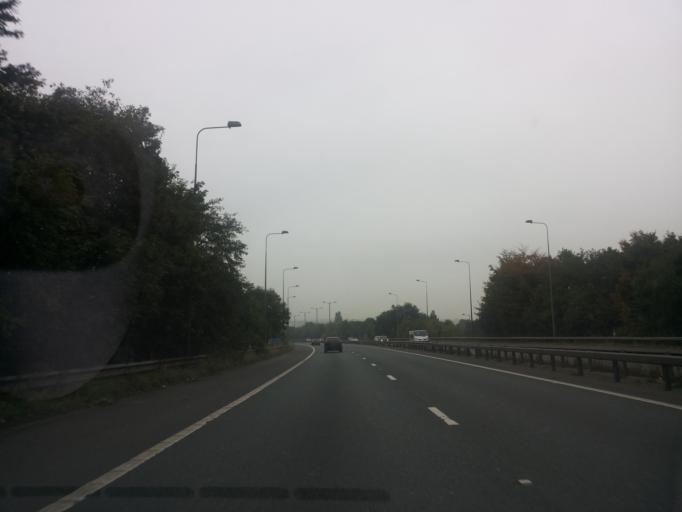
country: GB
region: England
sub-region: Borough of Bury
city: Bury
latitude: 53.5925
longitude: -2.2714
